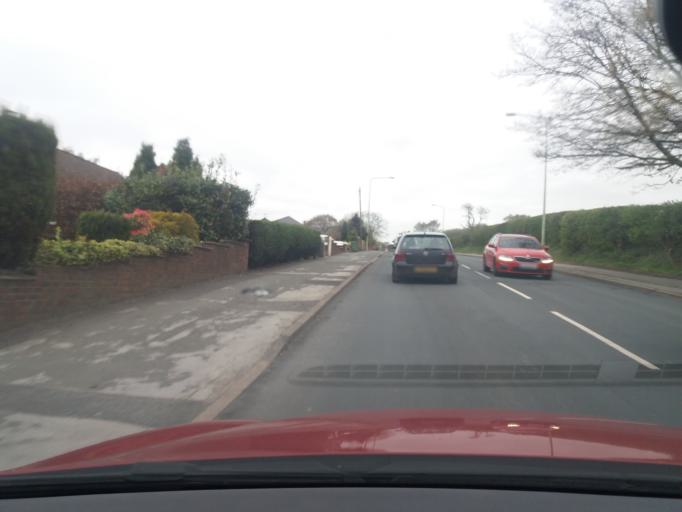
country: GB
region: England
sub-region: Lancashire
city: Chorley
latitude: 53.6661
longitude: -2.6158
